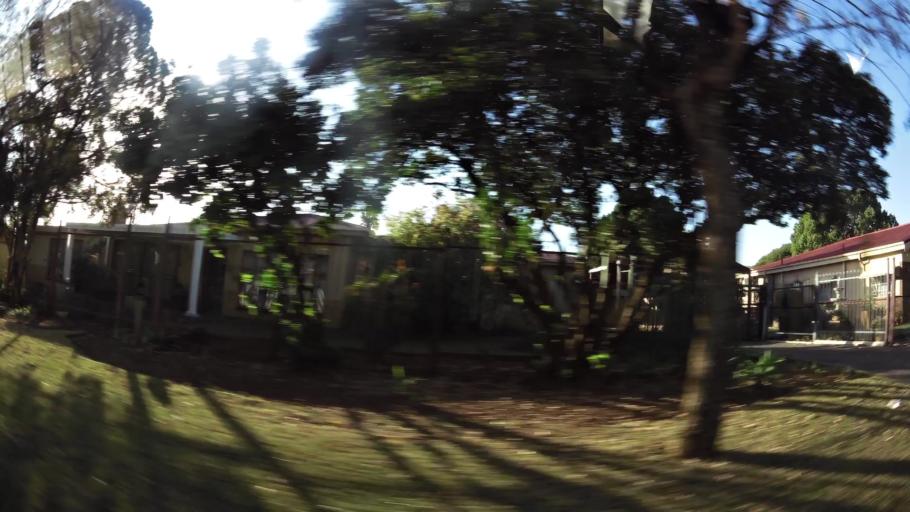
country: ZA
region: Gauteng
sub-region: City of Tshwane Metropolitan Municipality
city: Pretoria
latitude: -25.7048
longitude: 28.2037
